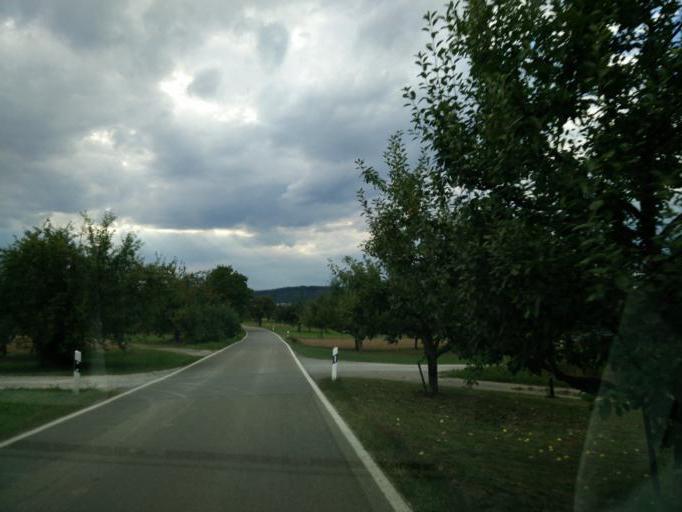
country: DE
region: Baden-Wuerttemberg
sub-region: Tuebingen Region
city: Sickenhausen
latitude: 48.5342
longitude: 9.1693
